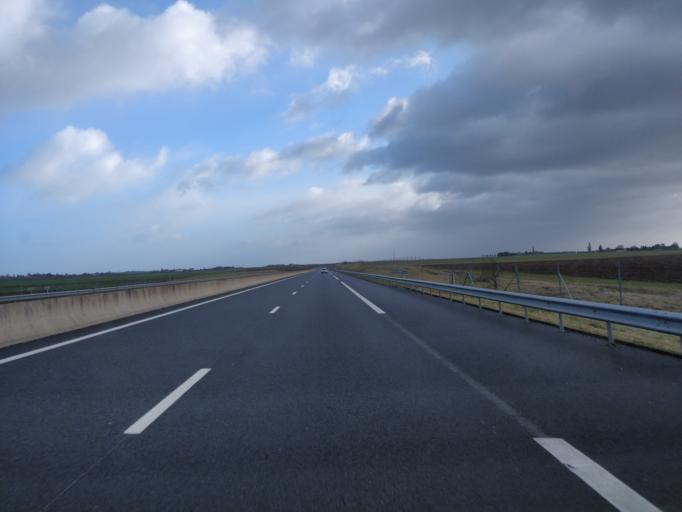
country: FR
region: Centre
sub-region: Departement du Loiret
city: Puiseaux
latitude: 48.0993
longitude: 2.0434
